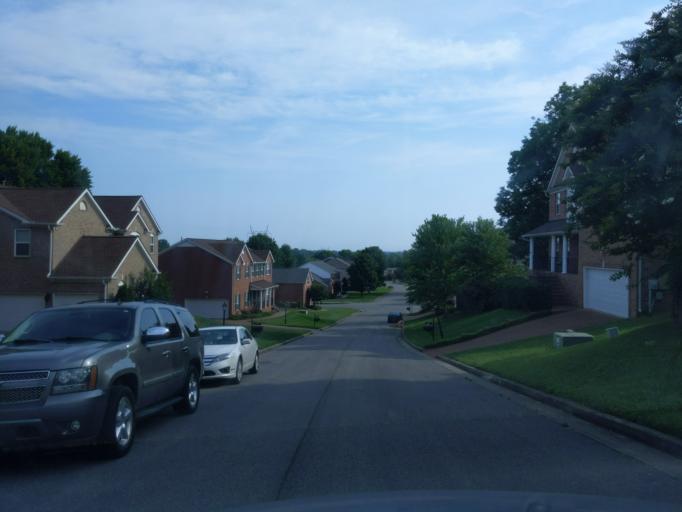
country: US
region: Tennessee
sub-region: Williamson County
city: Brentwood Estates
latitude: 36.0222
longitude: -86.7507
